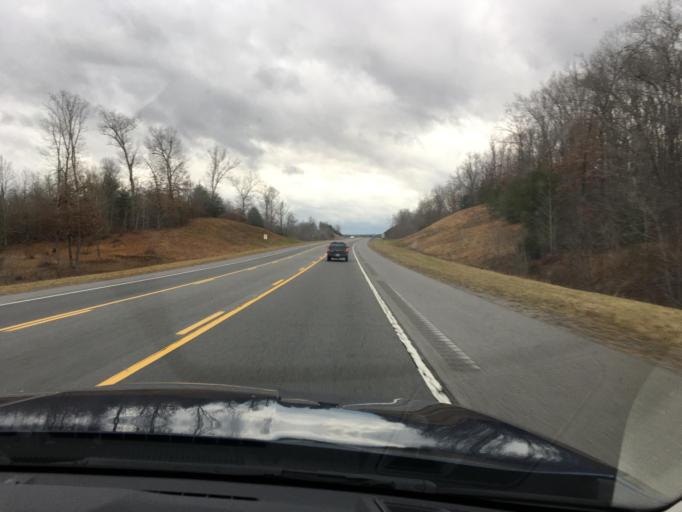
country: US
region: Tennessee
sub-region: Cumberland County
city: Crossville
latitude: 35.9442
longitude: -84.9939
